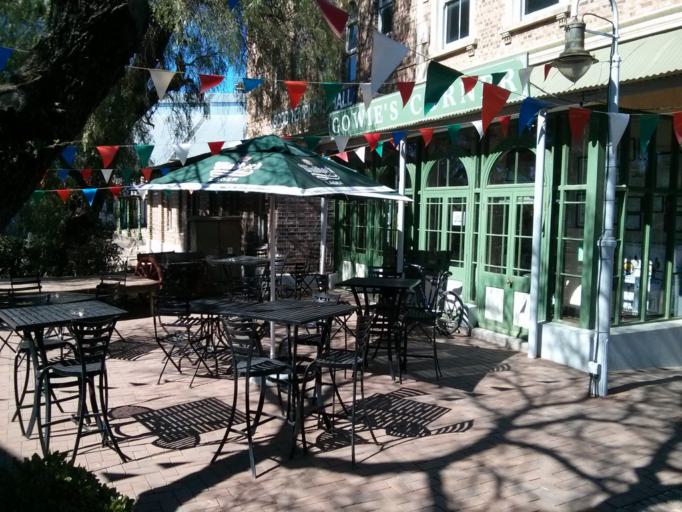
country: ZA
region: Northern Cape
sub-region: Frances Baard District Municipality
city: Kimberley
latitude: -28.7382
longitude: 24.7551
